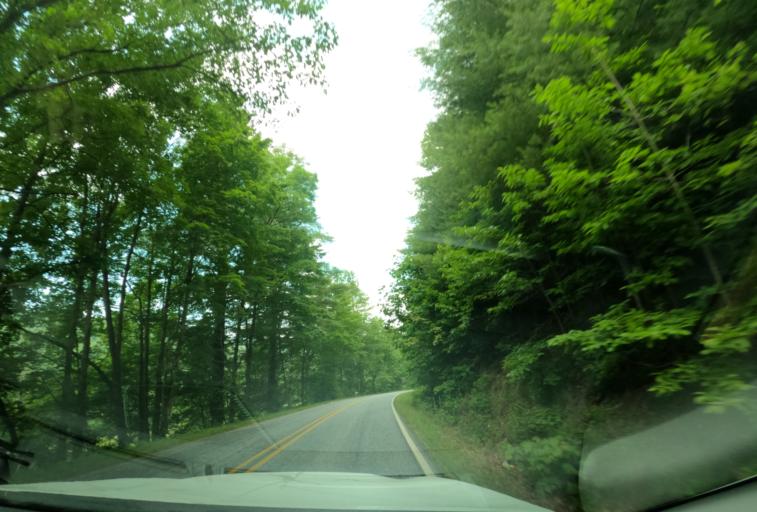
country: US
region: North Carolina
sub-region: Transylvania County
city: Brevard
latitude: 35.1830
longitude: -82.9268
